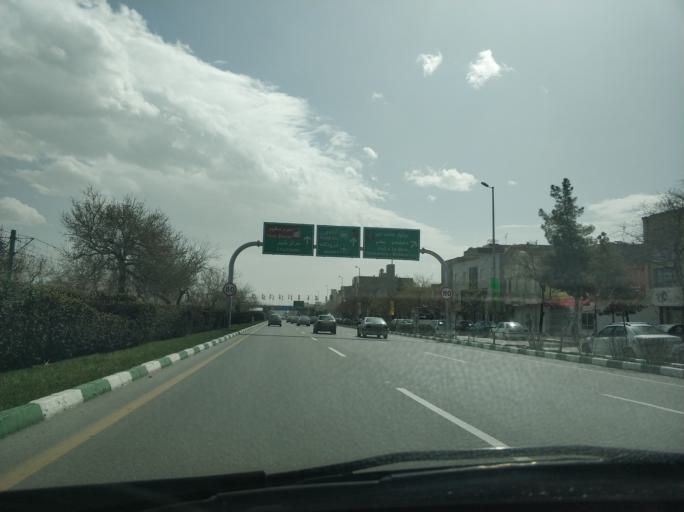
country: IR
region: Razavi Khorasan
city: Mashhad
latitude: 36.3283
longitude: 59.4978
